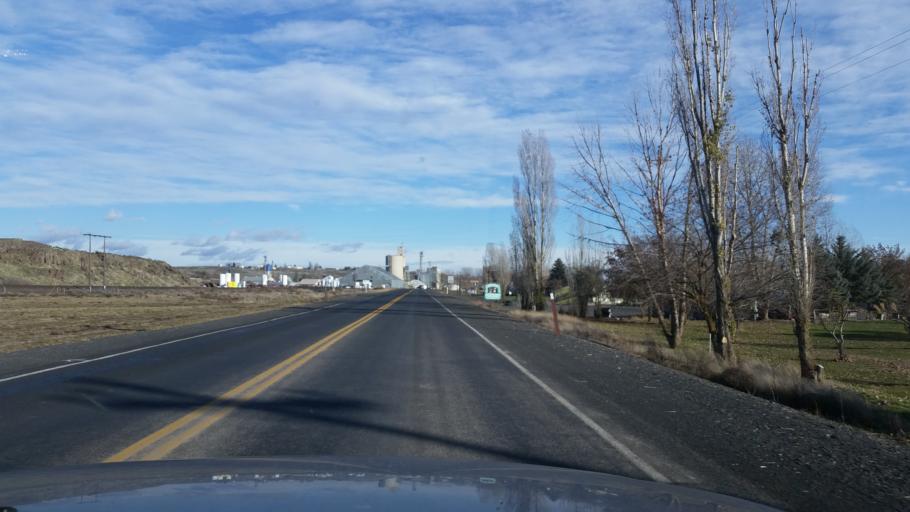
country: US
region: Washington
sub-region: Adams County
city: Ritzville
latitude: 47.3314
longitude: -118.7027
